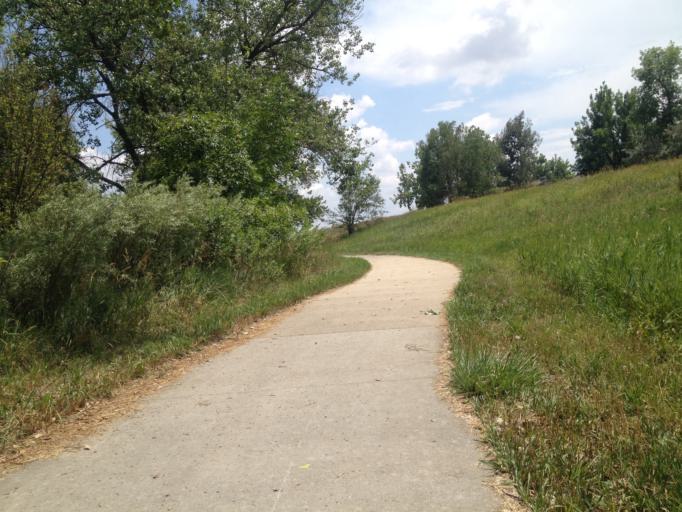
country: US
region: Colorado
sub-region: Boulder County
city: Louisville
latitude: 39.9721
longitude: -105.1482
